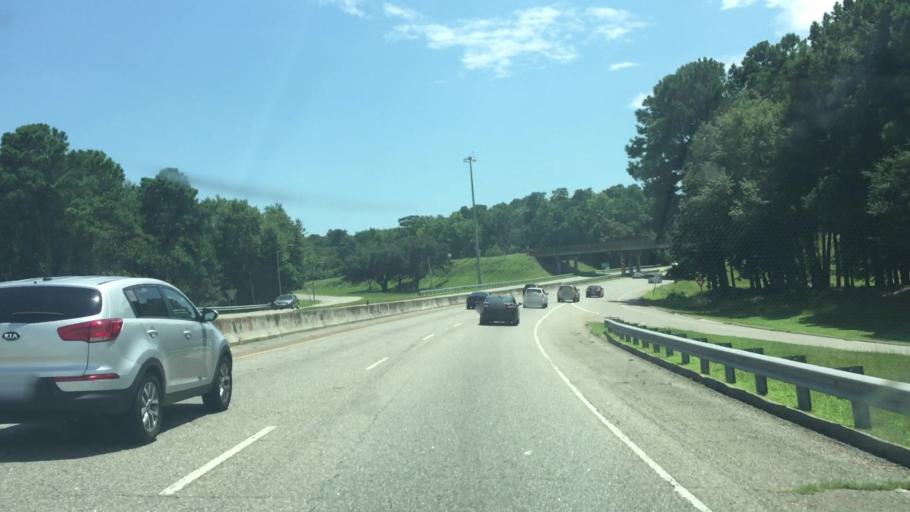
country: US
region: South Carolina
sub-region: Horry County
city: North Myrtle Beach
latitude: 33.8493
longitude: -78.6527
